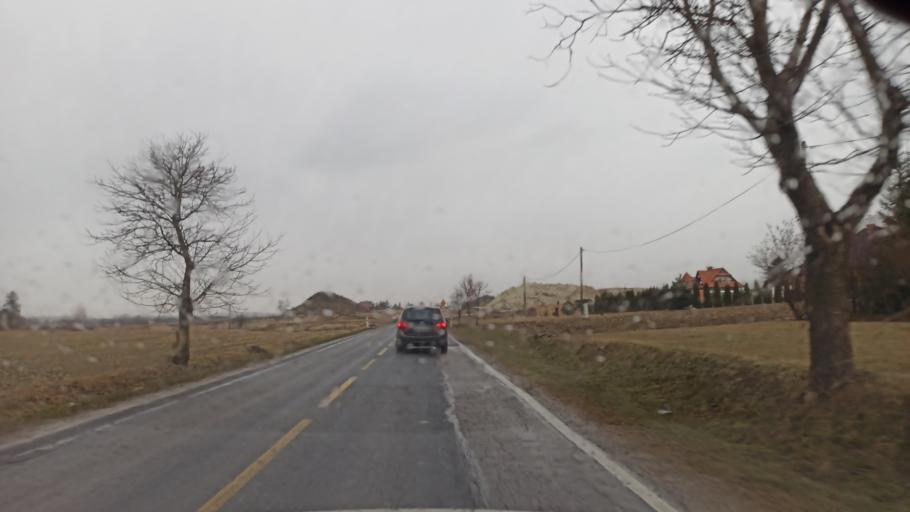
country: PL
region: Lublin Voivodeship
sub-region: Powiat lubelski
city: Niedrzwica Duza
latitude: 51.0991
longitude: 22.4090
